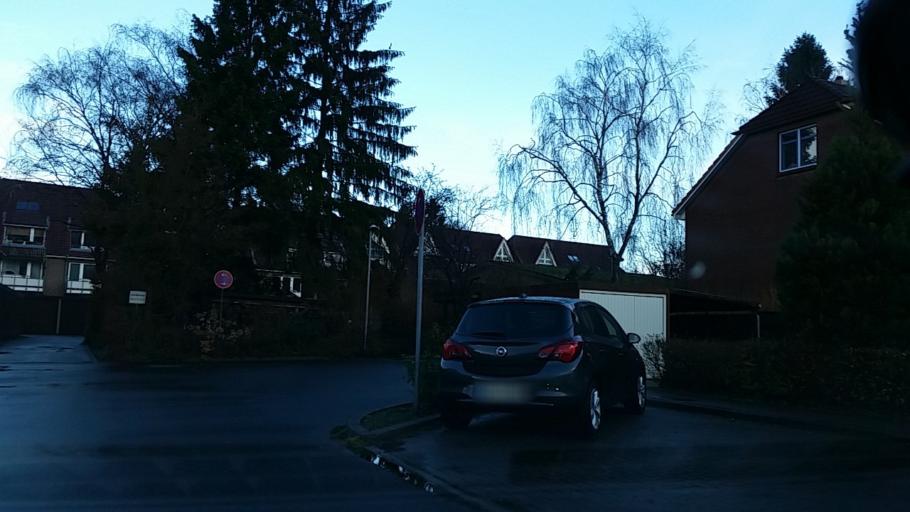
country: DE
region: Schleswig-Holstein
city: Halstenbek
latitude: 53.5846
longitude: 9.8244
